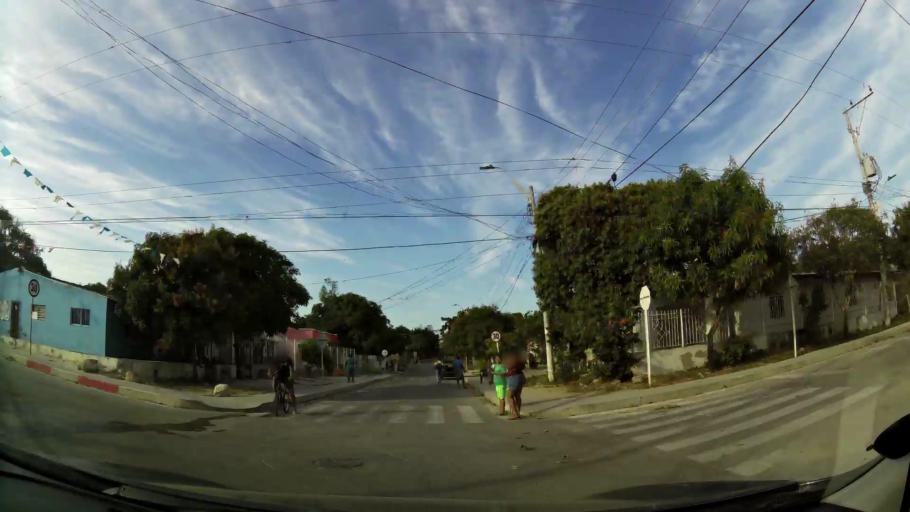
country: CO
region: Atlantico
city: Barranquilla
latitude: 10.9384
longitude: -74.8225
